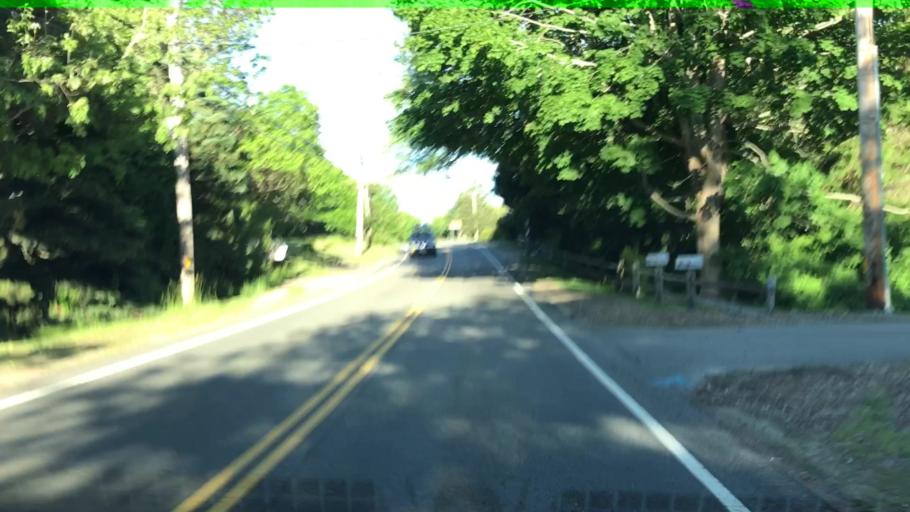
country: US
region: Massachusetts
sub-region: Barnstable County
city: East Harwich
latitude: 41.6999
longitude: -70.0197
